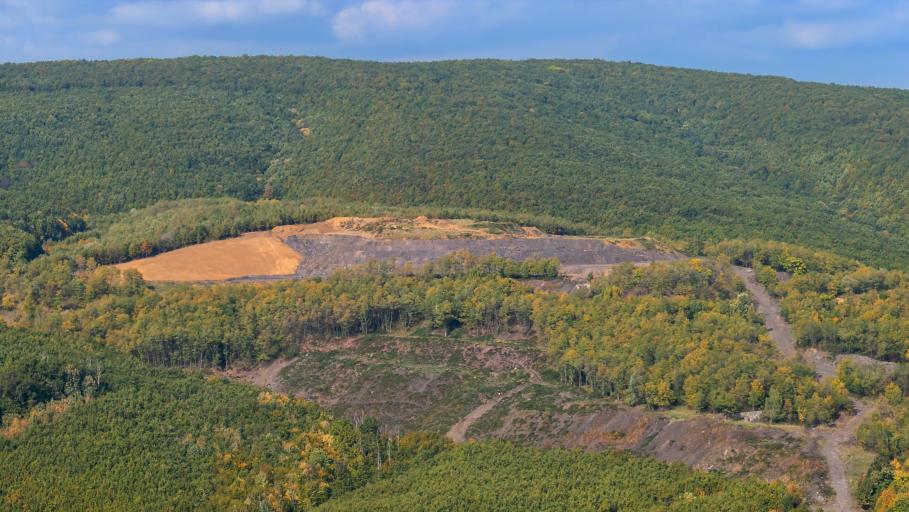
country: HU
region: Baranya
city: Pecs
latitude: 46.0996
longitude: 18.2337
